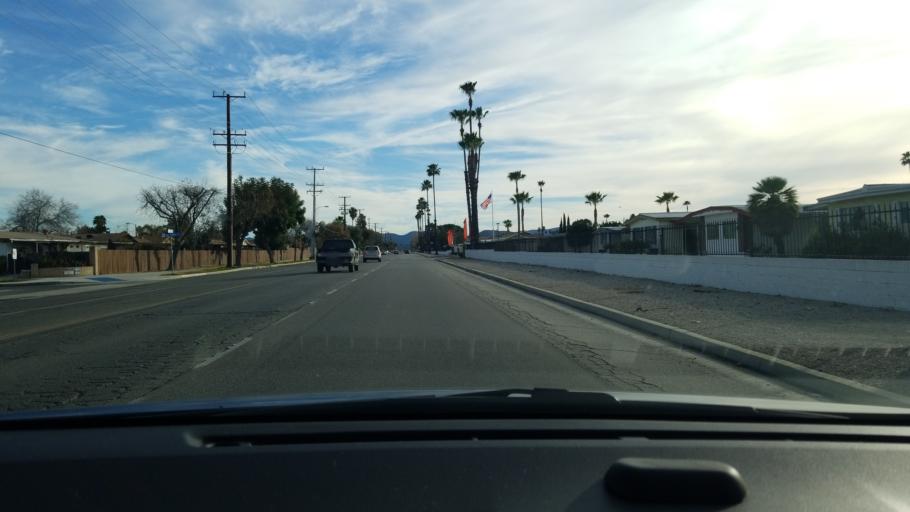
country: US
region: California
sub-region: Riverside County
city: Hemet
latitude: 33.7571
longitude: -116.9980
